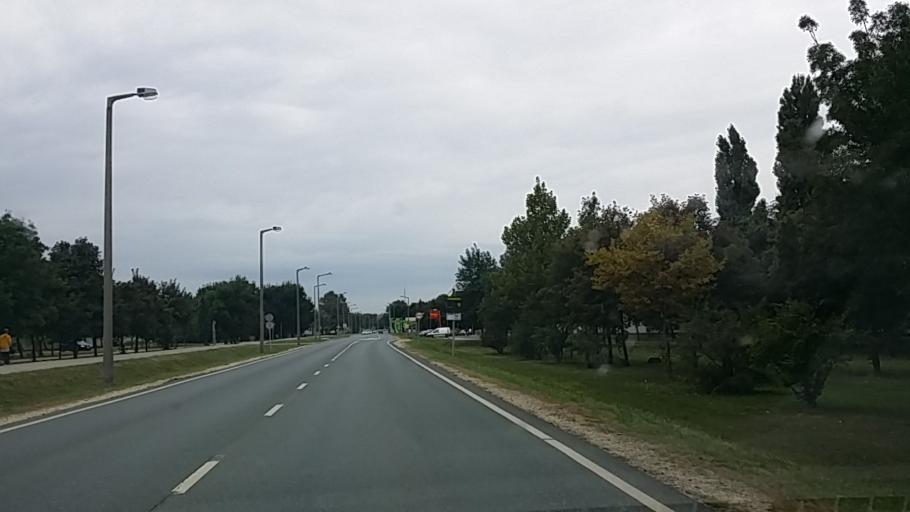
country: HU
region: Gyor-Moson-Sopron
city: Kapuvar
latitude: 47.5917
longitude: 17.0375
